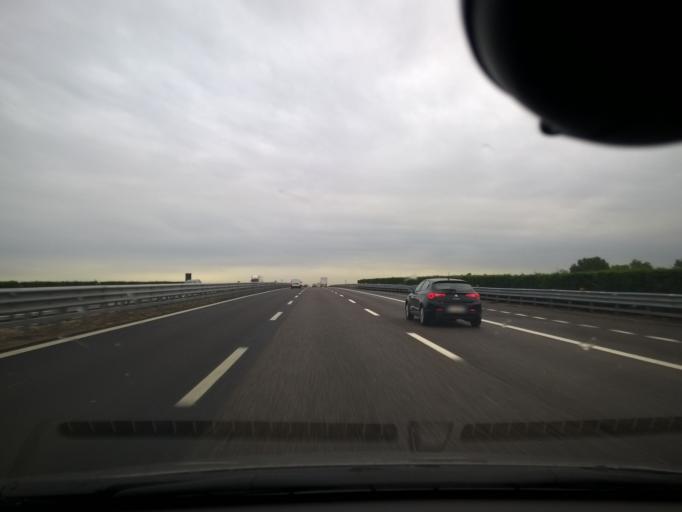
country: IT
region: Veneto
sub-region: Provincia di Vicenza
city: Grisignano di Zocco
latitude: 45.4865
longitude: 11.6828
